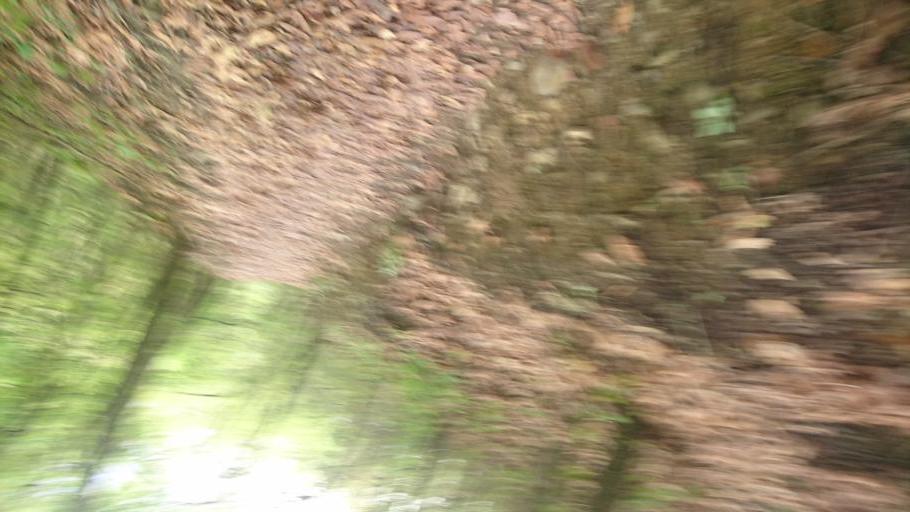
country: MX
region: Nuevo Leon
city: Garza Garcia
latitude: 25.6021
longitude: -100.3373
